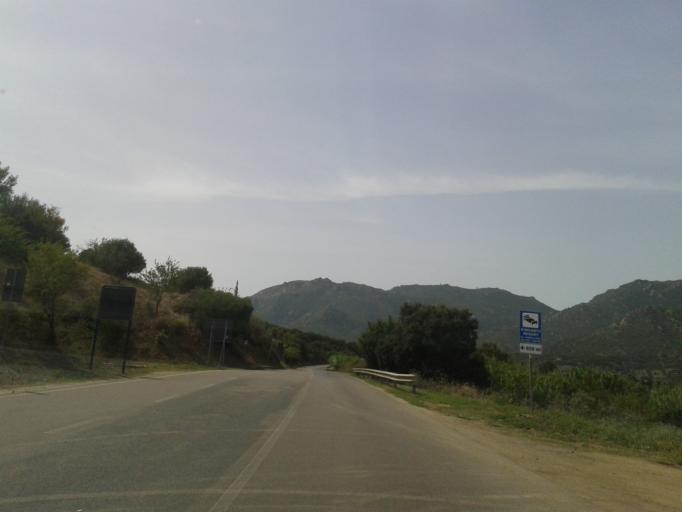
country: IT
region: Sardinia
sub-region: Provincia di Cagliari
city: Villasimius
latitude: 39.1457
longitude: 9.5102
